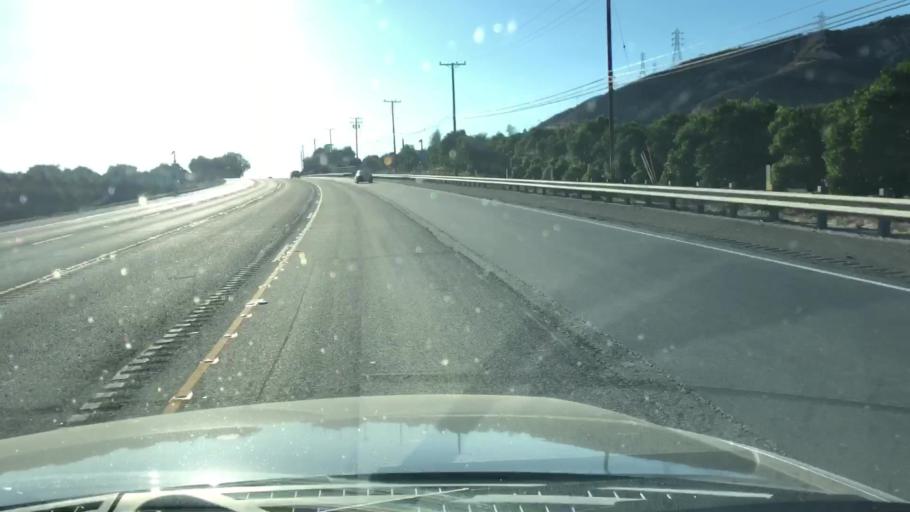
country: US
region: California
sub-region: Ventura County
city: Fillmore
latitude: 34.3971
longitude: -118.8566
